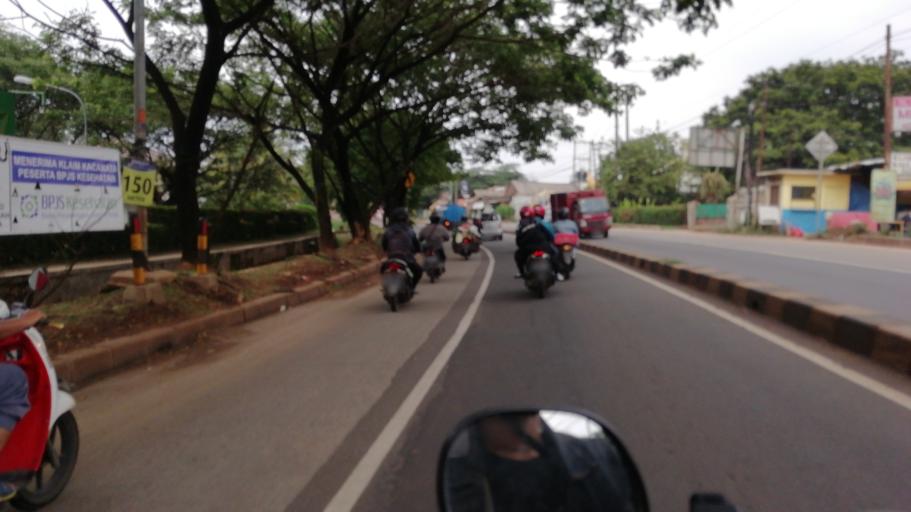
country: ID
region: West Java
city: Parung
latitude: -6.4729
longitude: 106.7291
